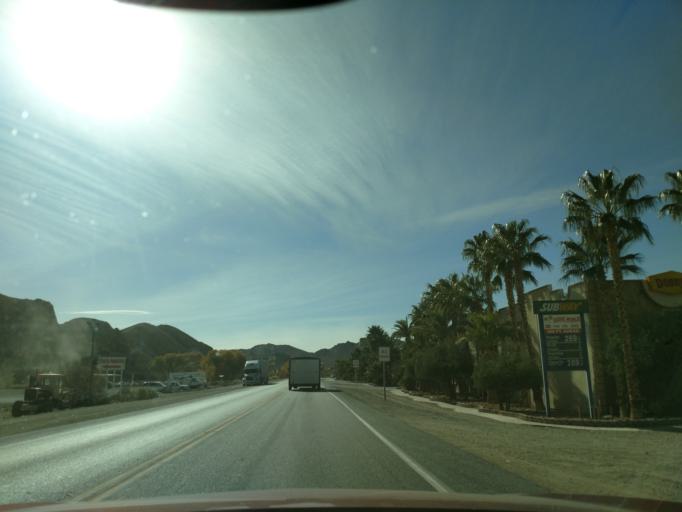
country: US
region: Nevada
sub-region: Nye County
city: Beatty
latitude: 36.9151
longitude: -116.7523
